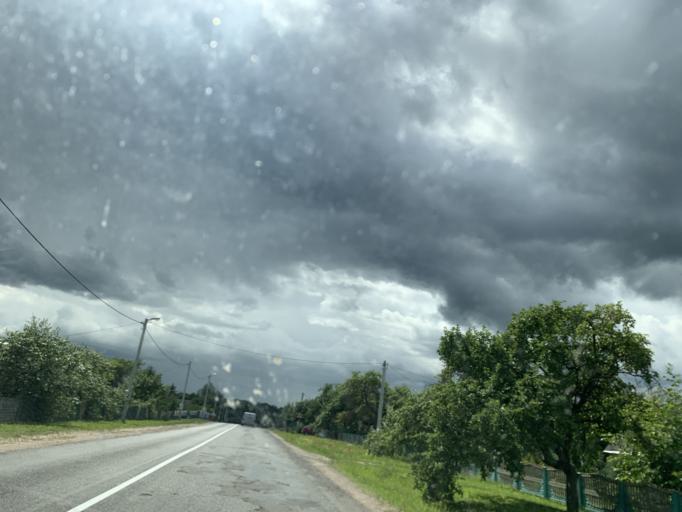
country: BY
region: Minsk
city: Ivyanyets
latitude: 53.9711
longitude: 26.8403
